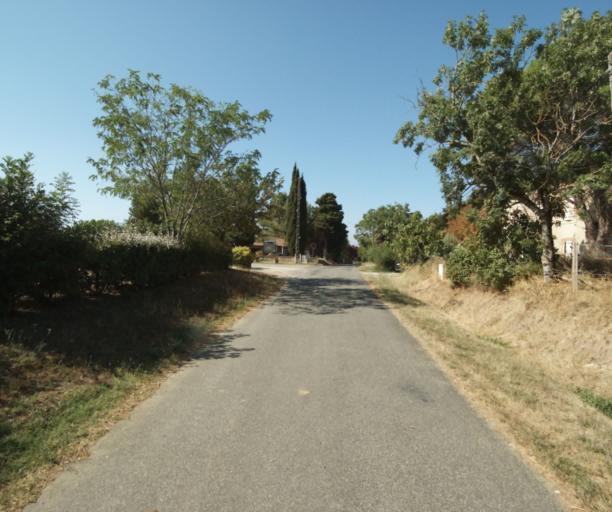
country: FR
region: Midi-Pyrenees
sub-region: Departement de la Haute-Garonne
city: Saint-Felix-Lauragais
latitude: 43.4940
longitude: 1.9290
